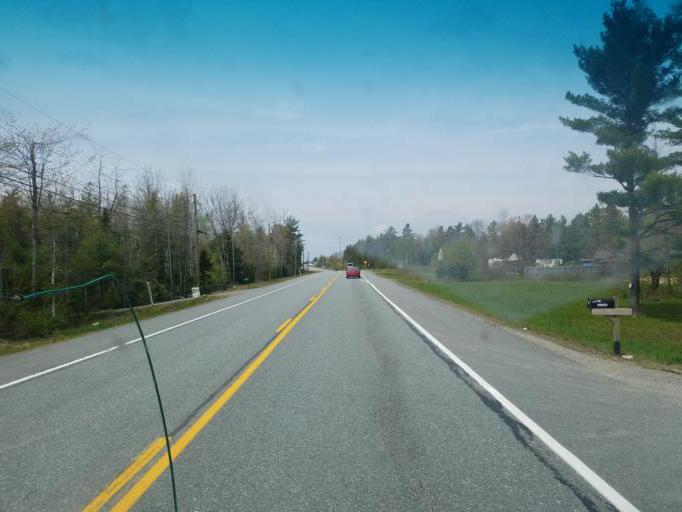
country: US
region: Maine
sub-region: Hancock County
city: Surry
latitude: 44.6106
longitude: -68.5207
